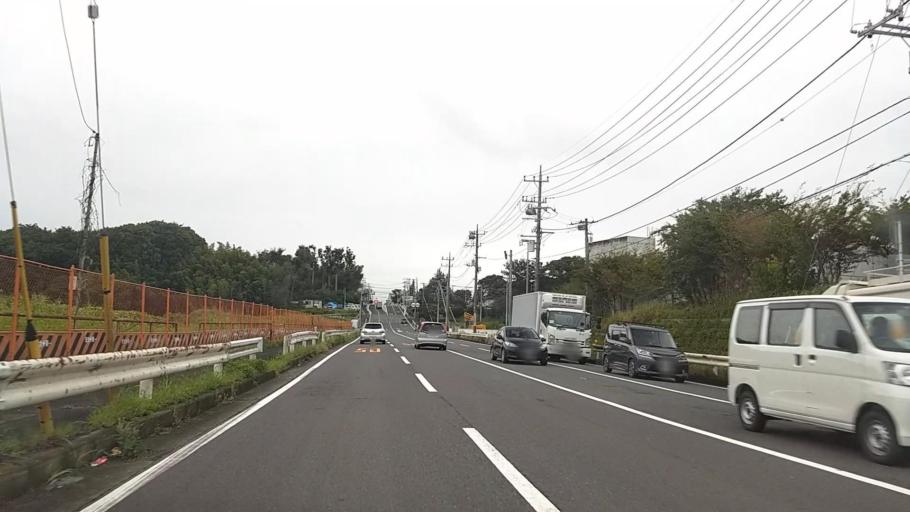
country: JP
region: Kanagawa
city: Fujisawa
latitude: 35.4073
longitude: 139.4566
